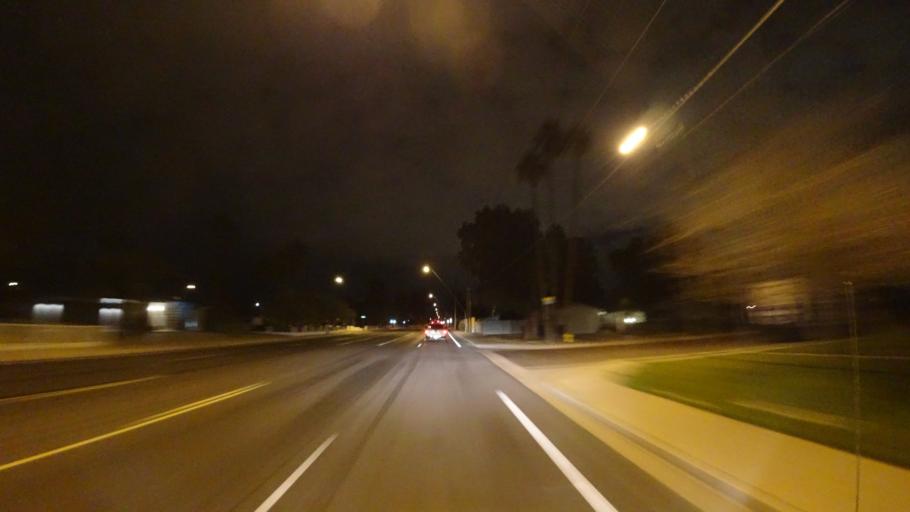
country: US
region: Arizona
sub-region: Maricopa County
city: Mesa
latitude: 33.4440
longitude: -111.8488
